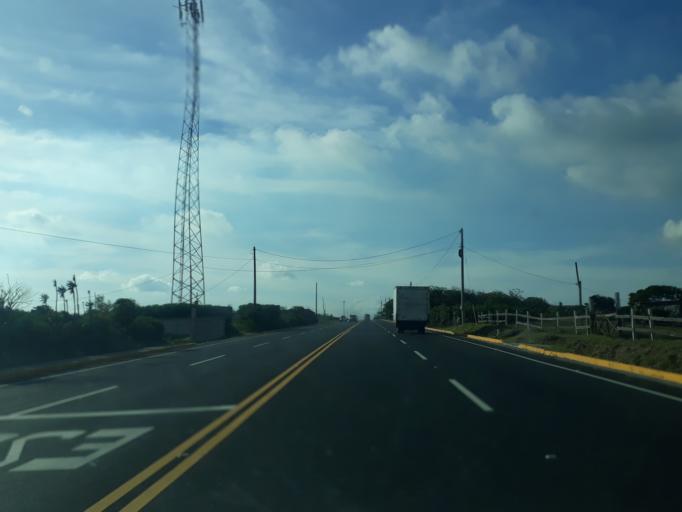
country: NI
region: Managua
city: El Crucero
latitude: 11.9256
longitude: -86.2836
